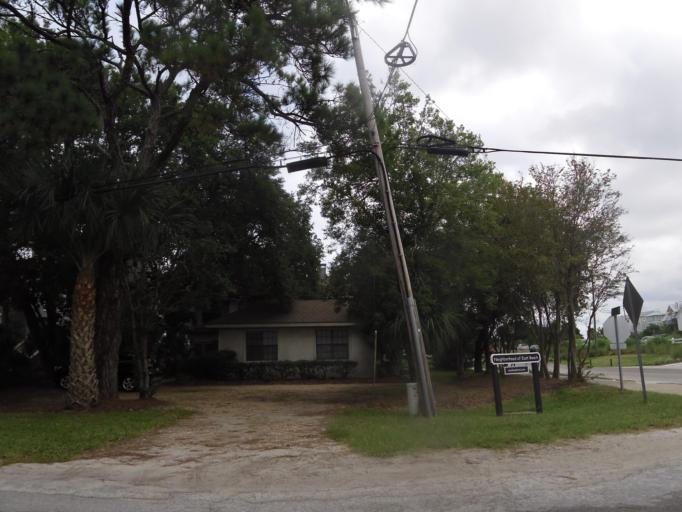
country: US
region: Georgia
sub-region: Glynn County
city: Saint Simons Island
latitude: 31.1463
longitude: -81.3733
